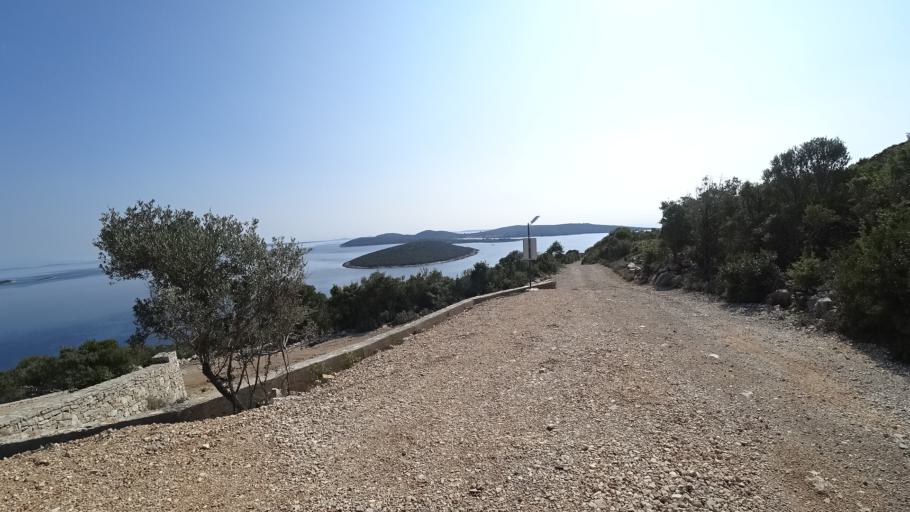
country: HR
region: Primorsko-Goranska
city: Mali Losinj
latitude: 44.4861
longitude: 14.5369
